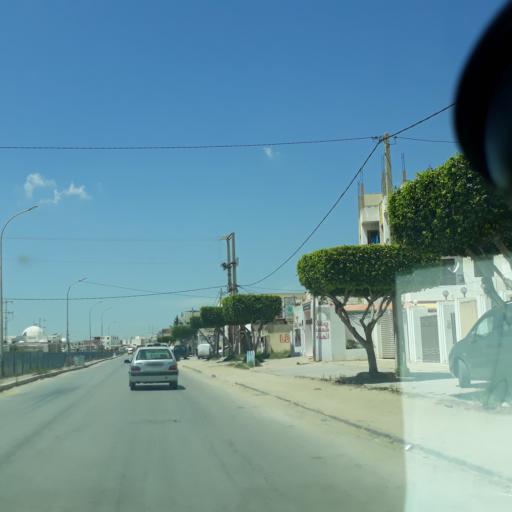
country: TN
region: Safaqis
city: Al Qarmadah
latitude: 34.8068
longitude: 10.7541
